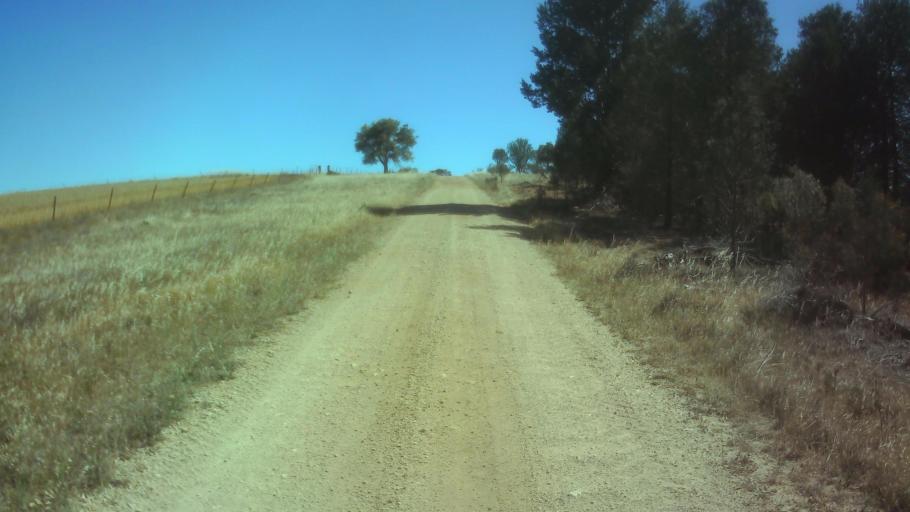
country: AU
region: New South Wales
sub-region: Weddin
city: Grenfell
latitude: -33.9705
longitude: 148.3438
